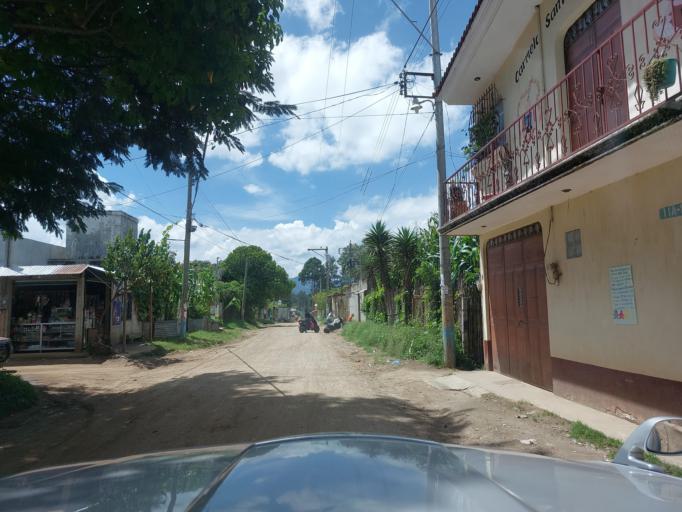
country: GT
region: Chimaltenango
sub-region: Municipio de Chimaltenango
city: Chimaltenango
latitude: 14.6463
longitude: -90.8150
